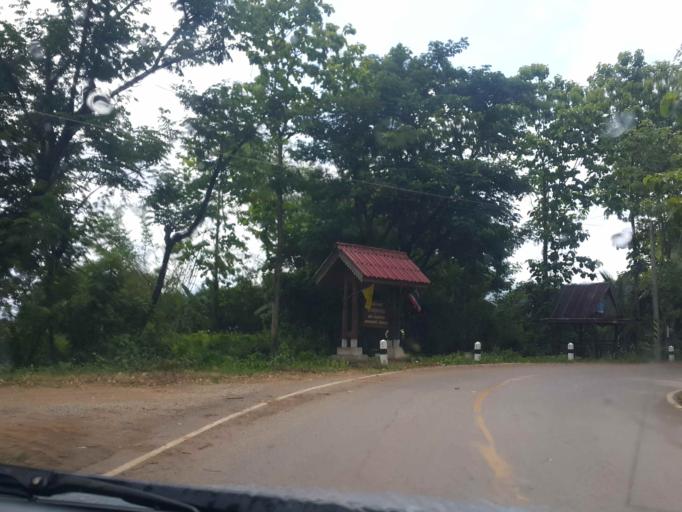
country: TH
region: Phayao
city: Dok Kham Tai
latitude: 19.0596
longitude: 100.0314
